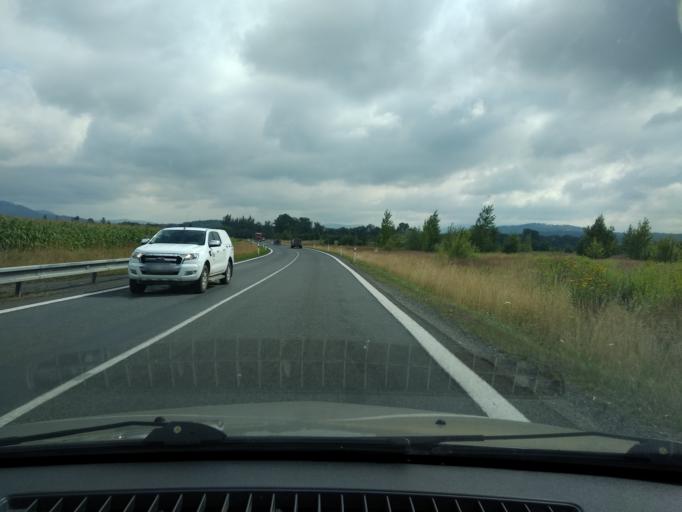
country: CZ
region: Olomoucky
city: Postrelmov
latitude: 49.9148
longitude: 16.9113
